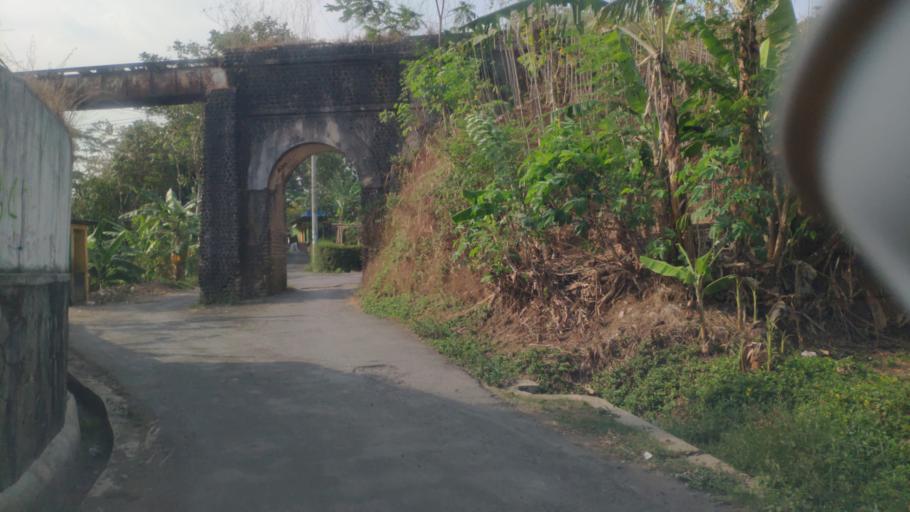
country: ID
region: Central Java
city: Wonosobo
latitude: -7.3921
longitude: 109.7169
